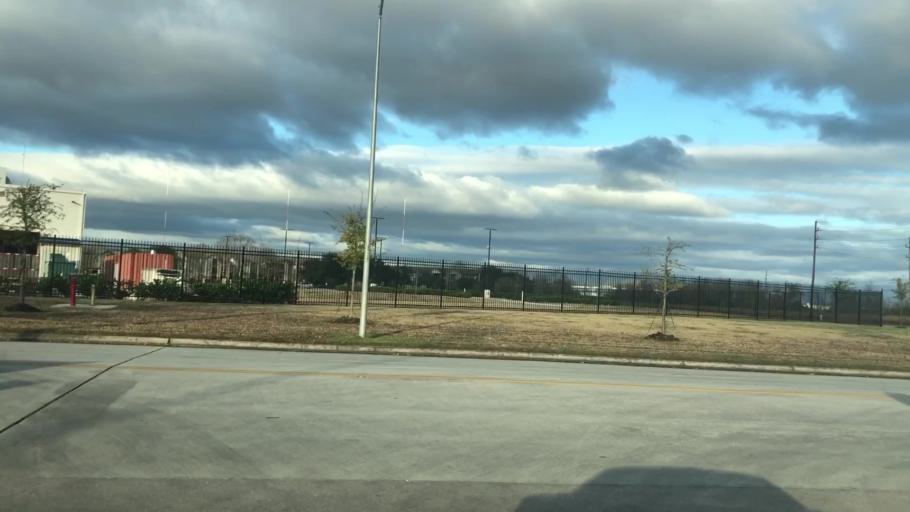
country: US
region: Texas
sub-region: Harris County
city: Aldine
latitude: 29.9175
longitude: -95.4167
